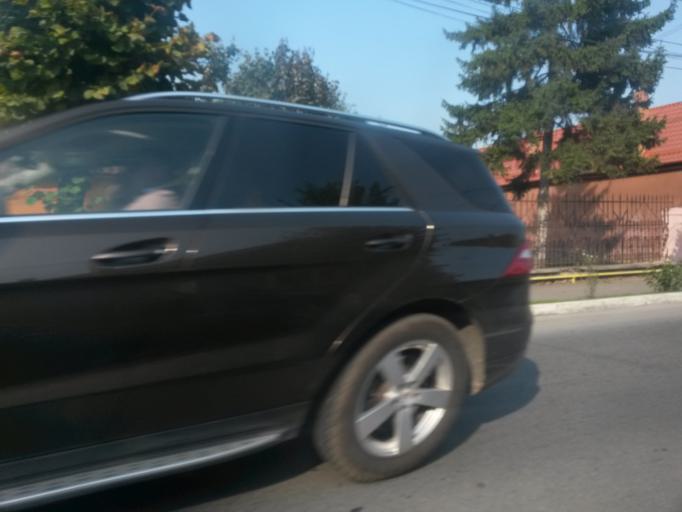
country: RO
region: Cluj
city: Turda
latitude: 46.5759
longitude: 23.7769
